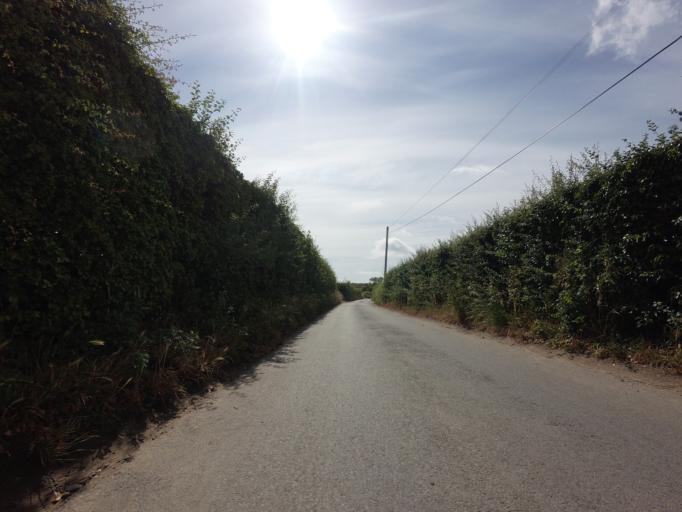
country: GB
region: England
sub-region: Greater London
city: Orpington
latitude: 51.3776
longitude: 0.1363
